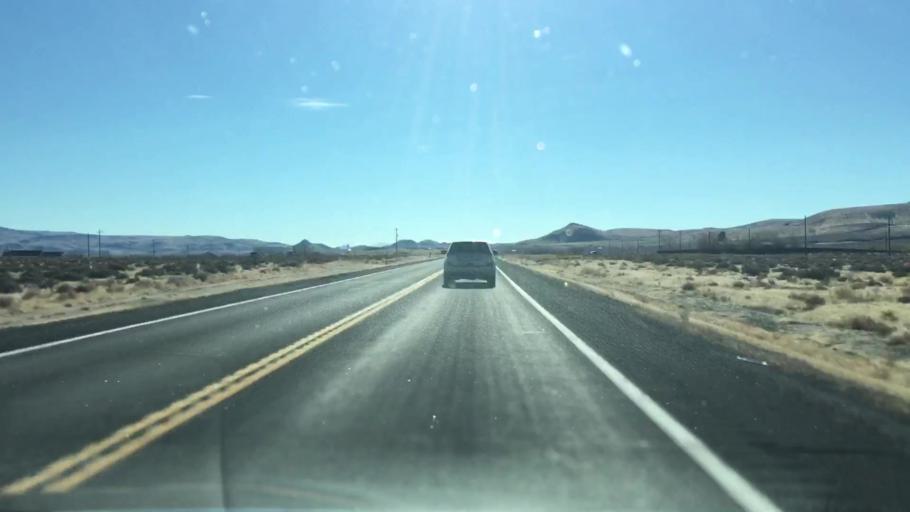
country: US
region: Nevada
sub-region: Lyon County
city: Silver Springs
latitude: 39.3710
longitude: -119.2345
